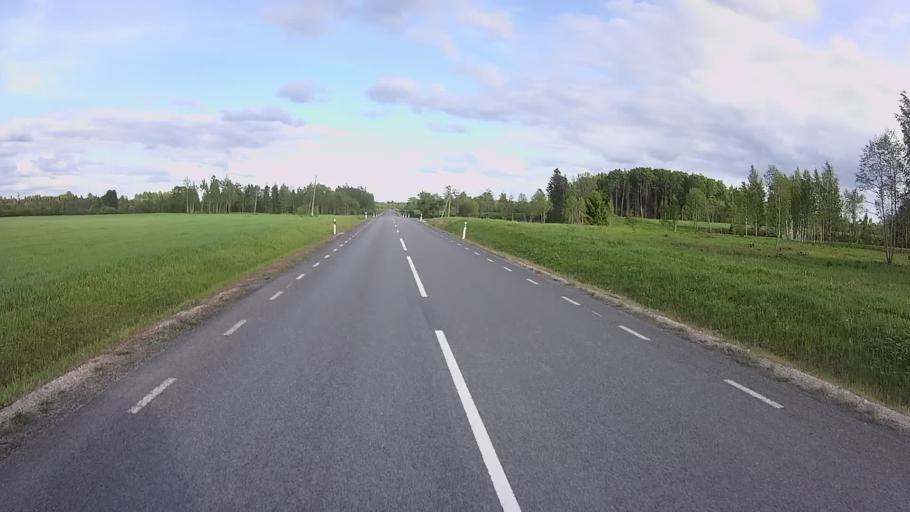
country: EE
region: Jogevamaa
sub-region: Mustvee linn
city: Mustvee
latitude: 59.0548
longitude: 27.0133
